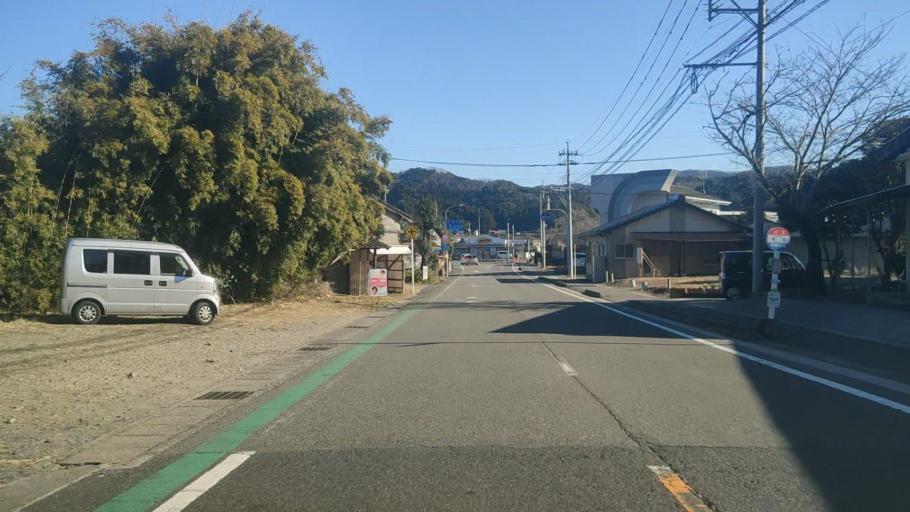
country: JP
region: Miyazaki
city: Nobeoka
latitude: 32.7060
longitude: 131.8172
